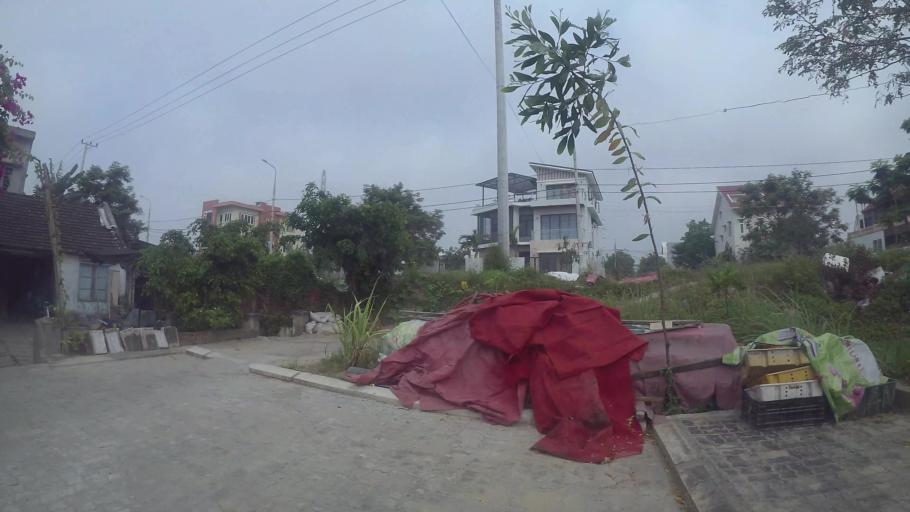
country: VN
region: Da Nang
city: Ngu Hanh Son
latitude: 16.0227
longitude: 108.2427
